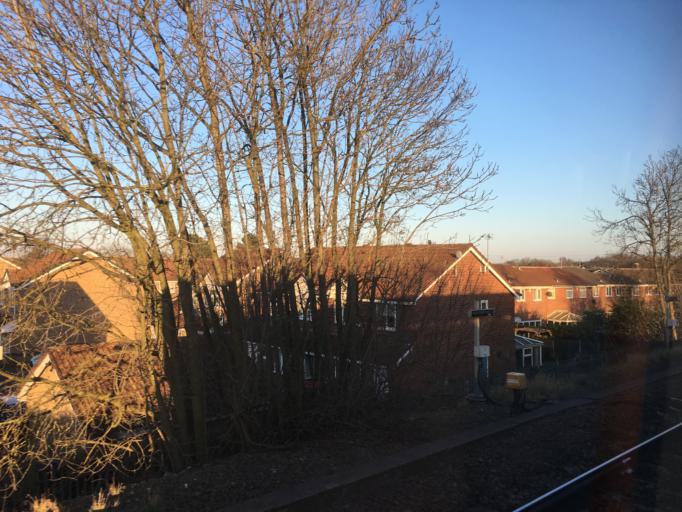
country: GB
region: England
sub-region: Derbyshire
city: Long Eaton
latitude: 52.8827
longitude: -1.2750
